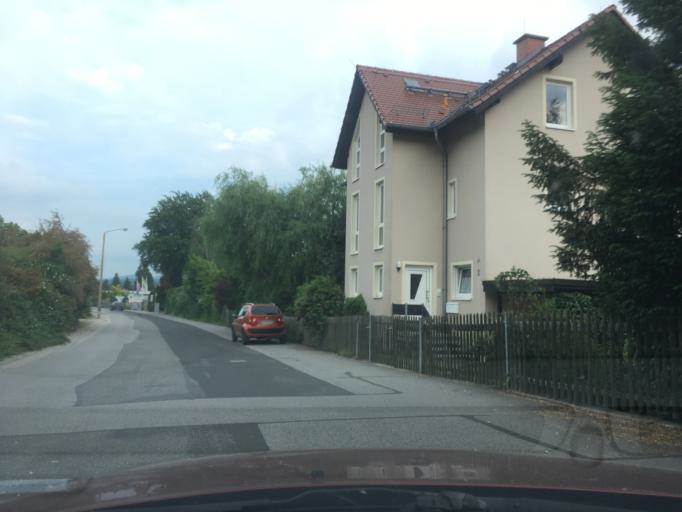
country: DE
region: Saxony
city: Bautzen
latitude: 51.1726
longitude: 14.4426
